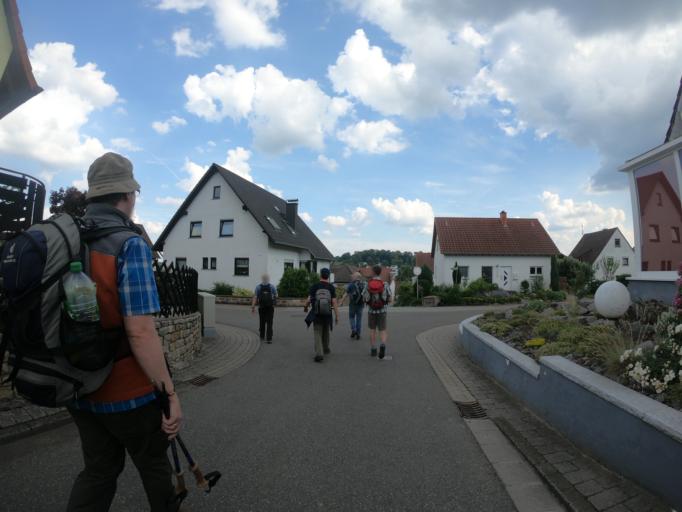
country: DE
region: Rheinland-Pfalz
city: Klingenmunster
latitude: 49.1422
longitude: 8.0129
